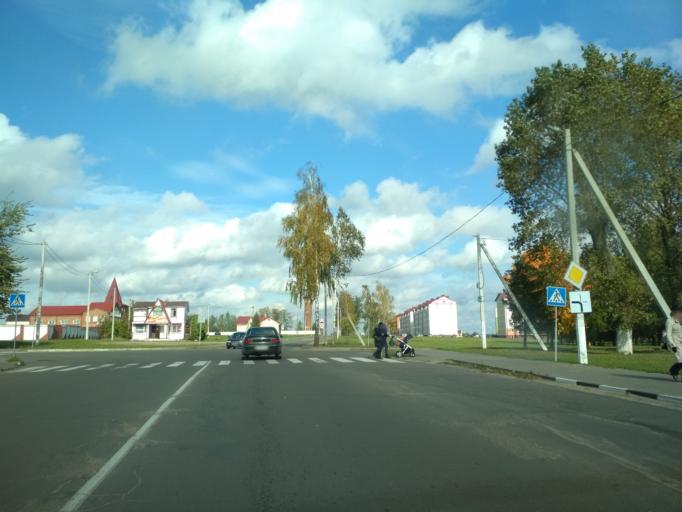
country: BY
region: Minsk
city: Mar''ina Horka
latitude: 53.5068
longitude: 28.1542
